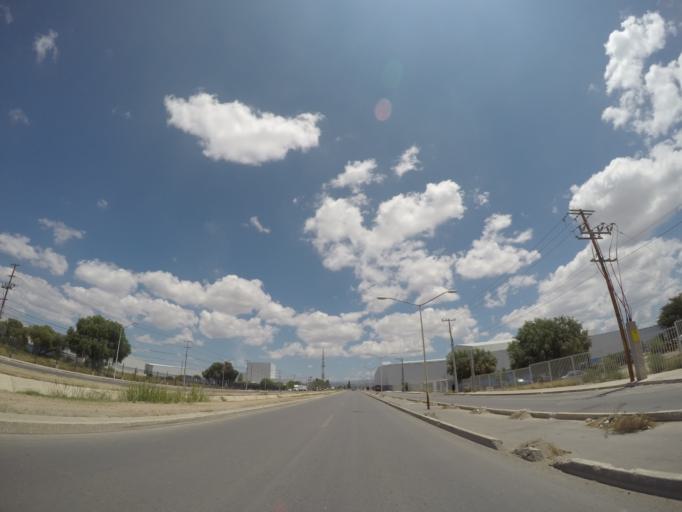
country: MX
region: San Luis Potosi
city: La Pila
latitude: 22.0494
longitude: -100.8686
